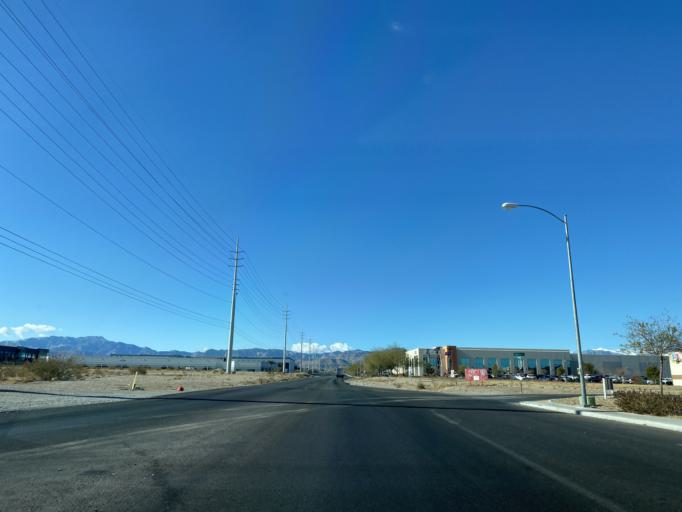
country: US
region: Nevada
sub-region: Clark County
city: Spring Valley
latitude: 36.0709
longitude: -115.2272
